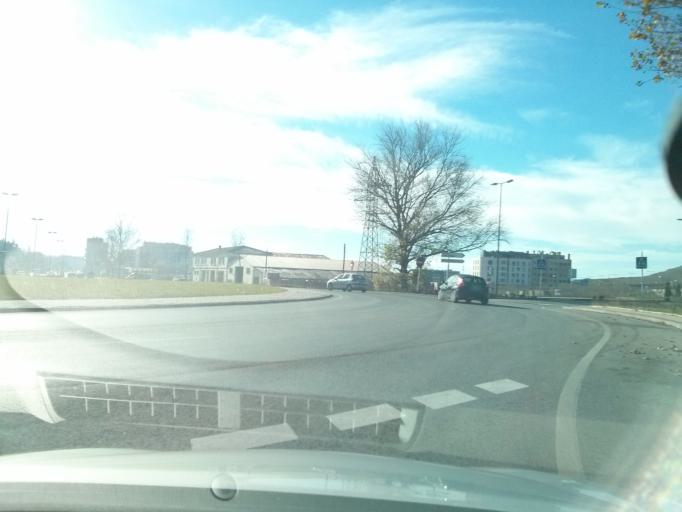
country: ES
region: Castille and Leon
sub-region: Provincia de Burgos
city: Burgos
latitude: 42.3532
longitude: -3.7111
